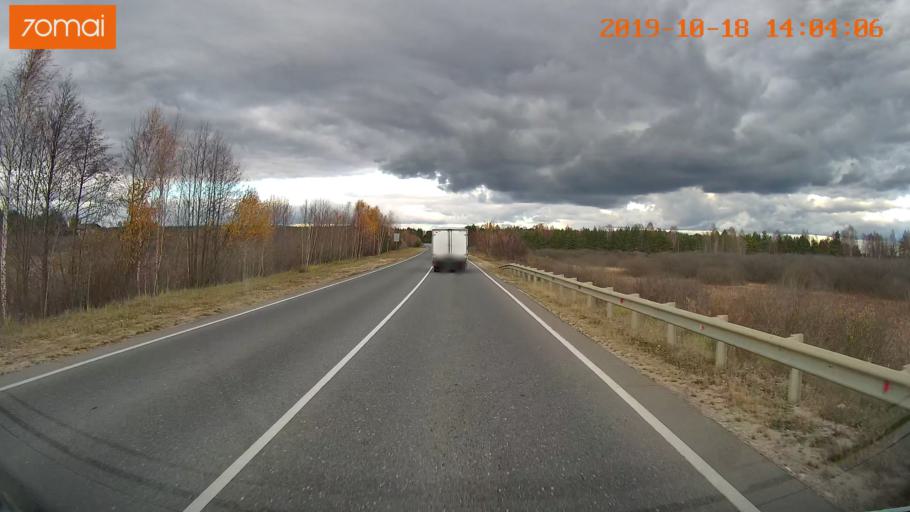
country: RU
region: Rjazan
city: Spas-Klepiki
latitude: 55.1222
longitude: 40.1334
